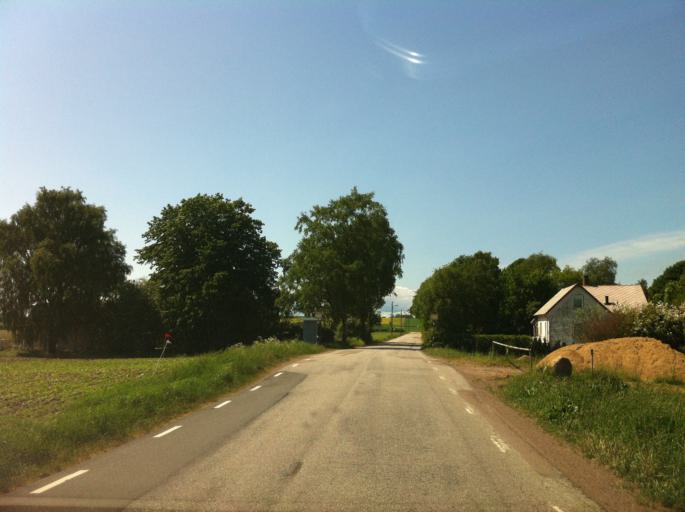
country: SE
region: Skane
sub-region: Landskrona
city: Asmundtorp
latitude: 55.9242
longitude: 12.9371
